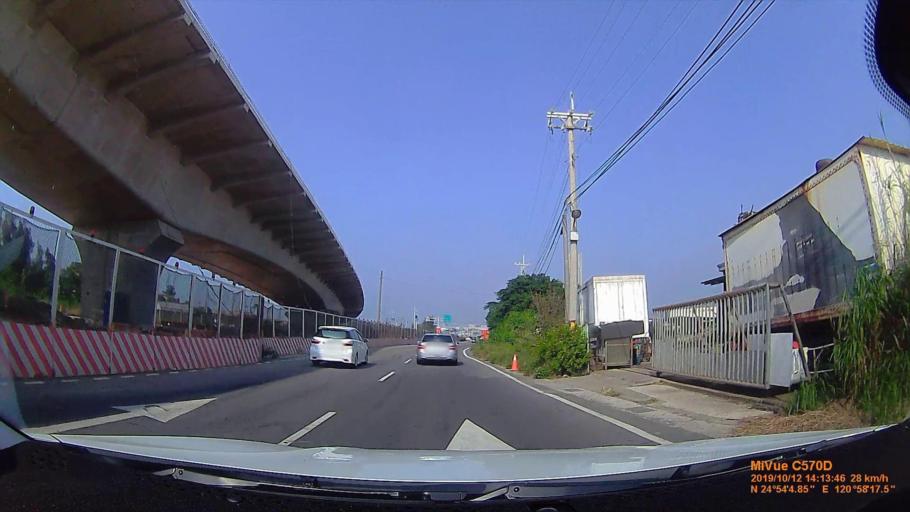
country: TW
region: Taiwan
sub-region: Hsinchu
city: Zhubei
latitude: 24.9042
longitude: 120.9739
